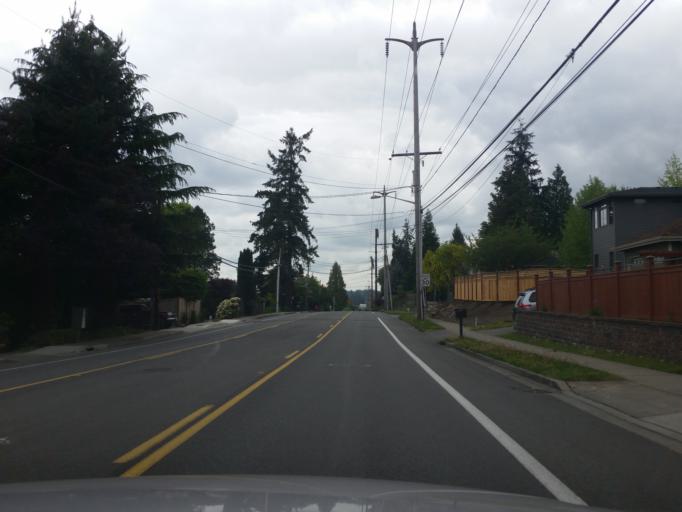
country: US
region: Washington
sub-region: King County
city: Kirkland
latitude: 47.6618
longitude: -122.1962
